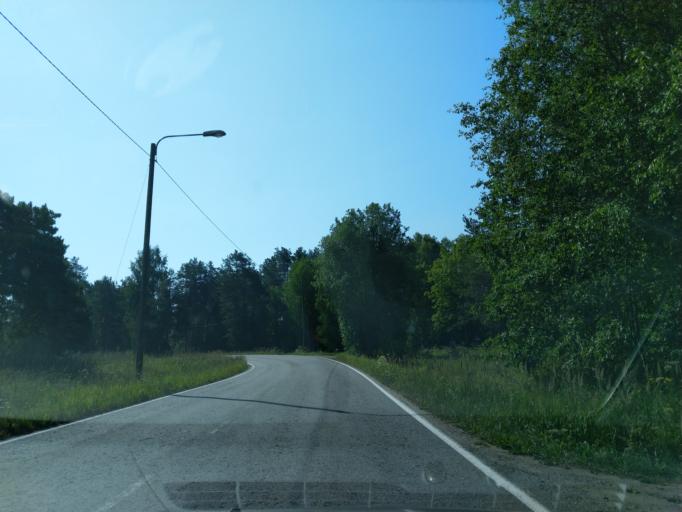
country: FI
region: Satakunta
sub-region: Pori
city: Noormarkku
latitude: 61.5871
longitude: 21.8954
